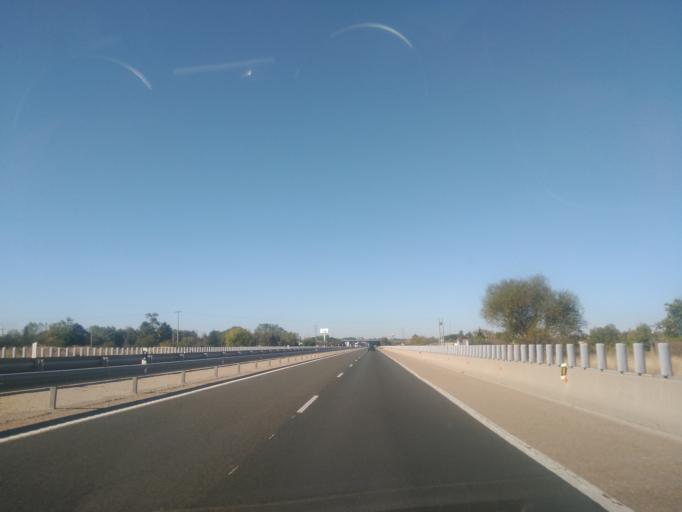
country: ES
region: Castille and Leon
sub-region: Provincia de Valladolid
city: Tudela de Duero
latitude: 41.5927
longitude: -4.5920
